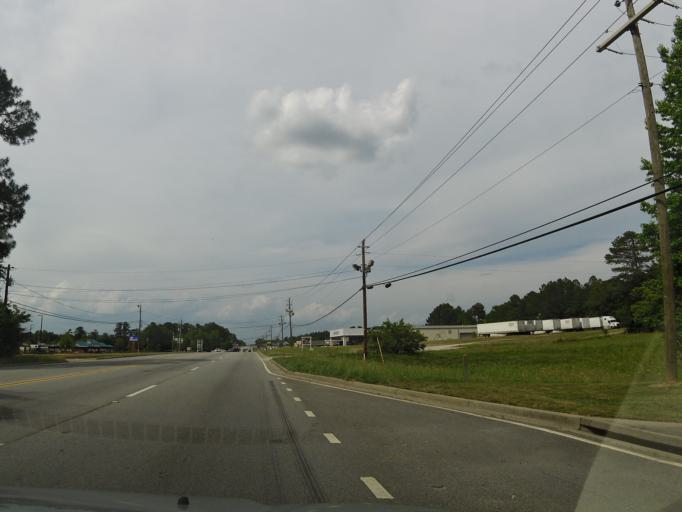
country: US
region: Georgia
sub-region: McDuffie County
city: Thomson
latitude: 33.4876
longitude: -82.5048
